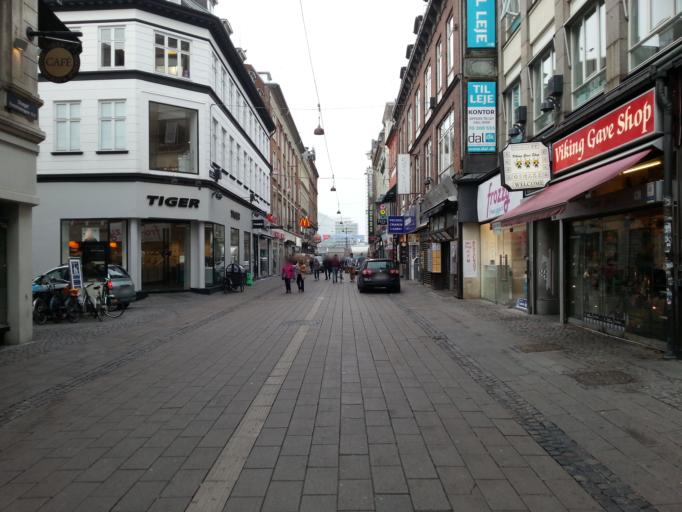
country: DK
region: Capital Region
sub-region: Kobenhavn
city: Copenhagen
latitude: 55.6771
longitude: 12.5707
